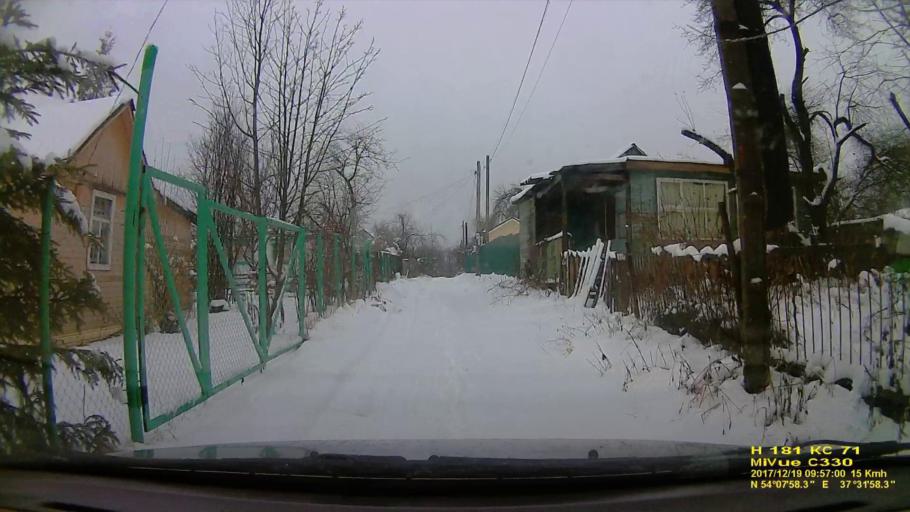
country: RU
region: Tula
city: Kosaya Gora
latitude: 54.1328
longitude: 37.5331
